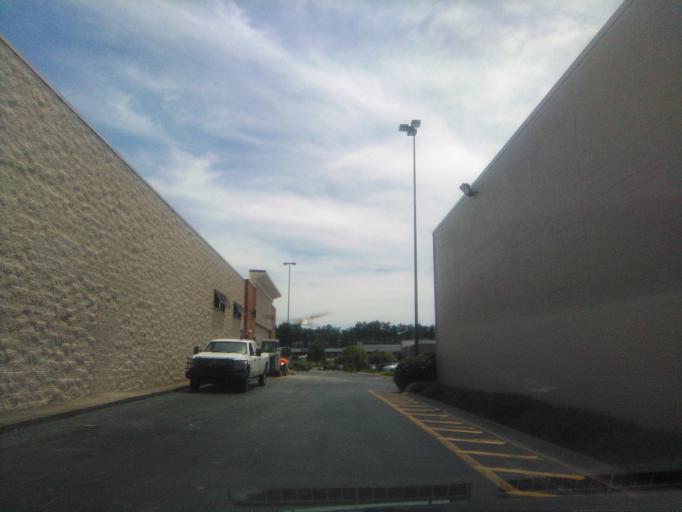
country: US
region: Tennessee
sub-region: Davidson County
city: Belle Meade
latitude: 36.1311
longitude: -86.8525
